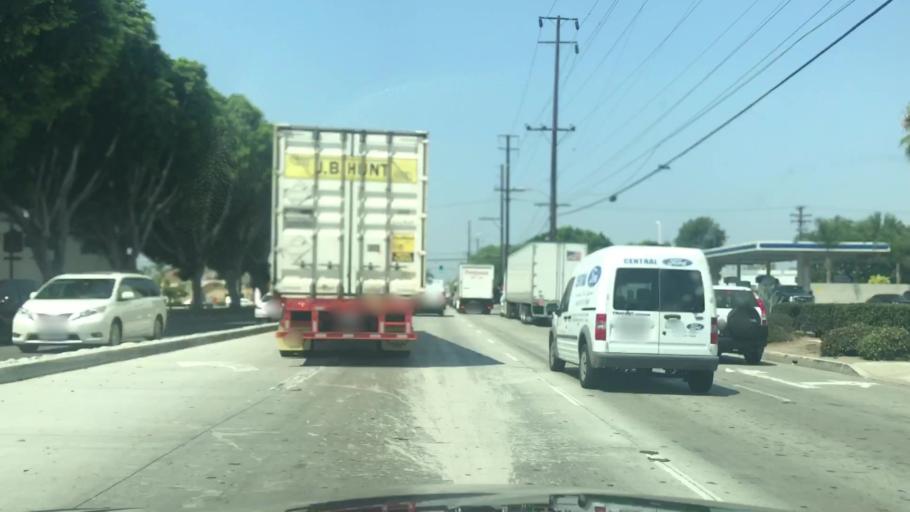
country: US
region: California
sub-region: Los Angeles County
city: La Mirada
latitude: 33.8880
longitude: -118.0274
